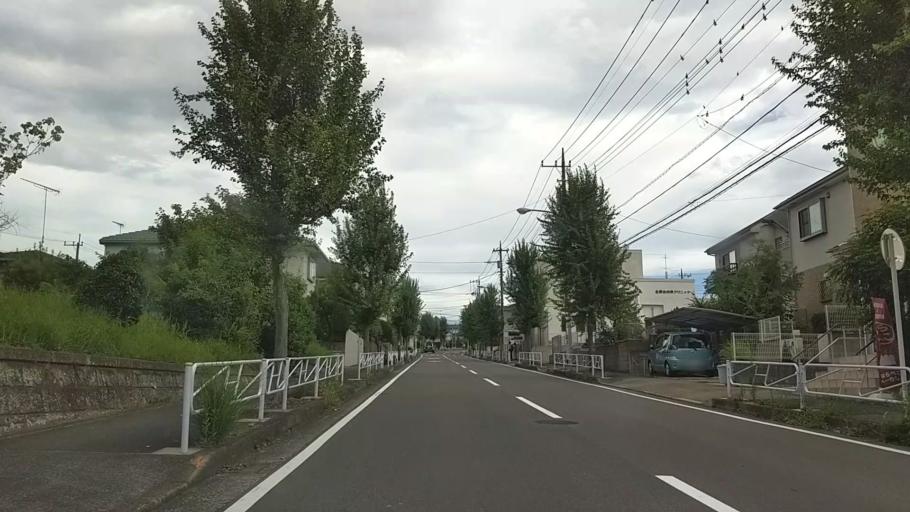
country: JP
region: Tokyo
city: Hachioji
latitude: 35.6346
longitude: 139.3564
